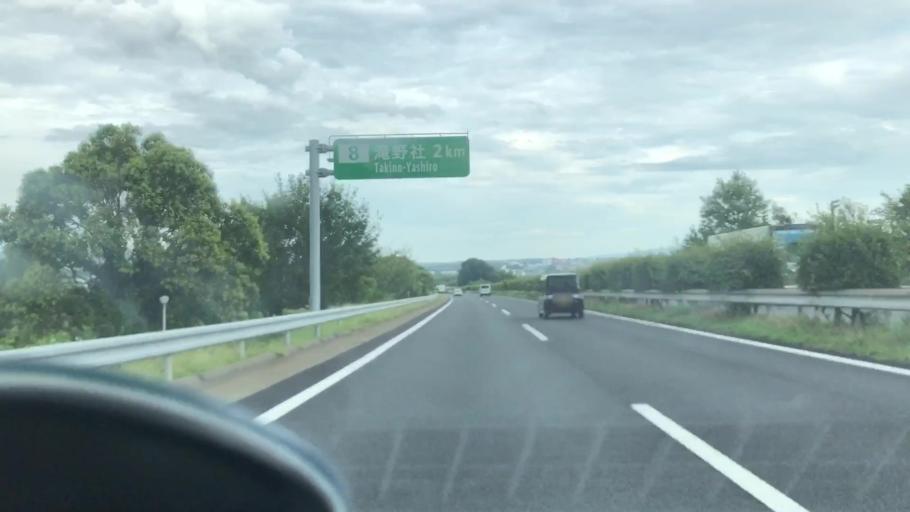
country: JP
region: Hyogo
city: Yashiro
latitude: 34.9302
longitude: 134.9376
